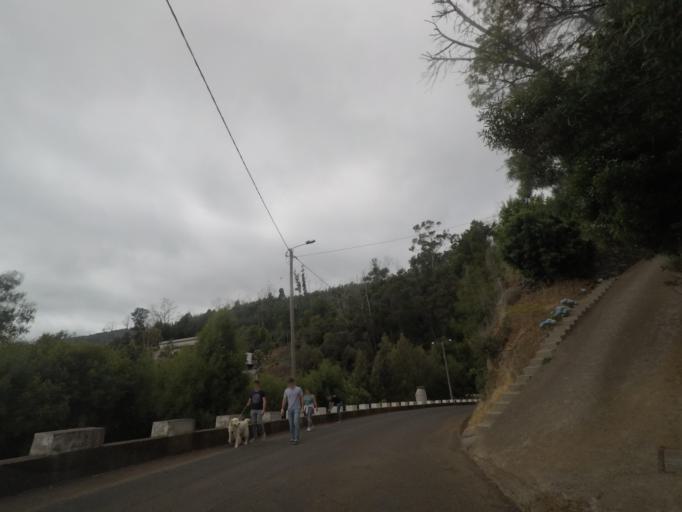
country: PT
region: Madeira
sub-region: Calheta
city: Estreito da Calheta
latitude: 32.7381
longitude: -17.1672
